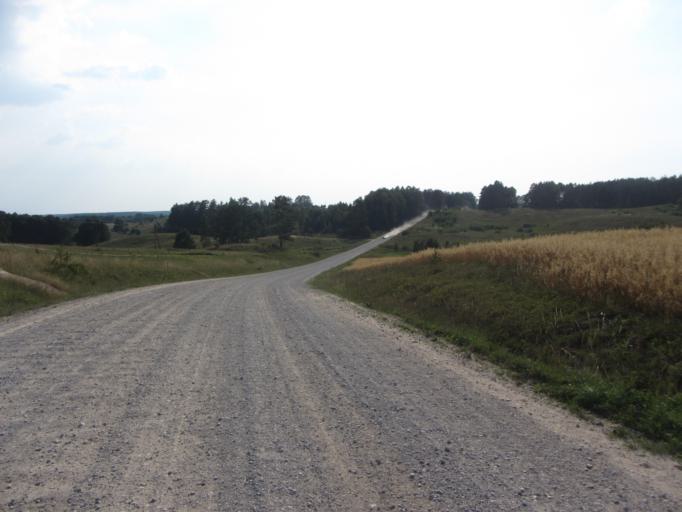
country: LT
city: Veisiejai
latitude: 54.0909
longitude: 23.6258
